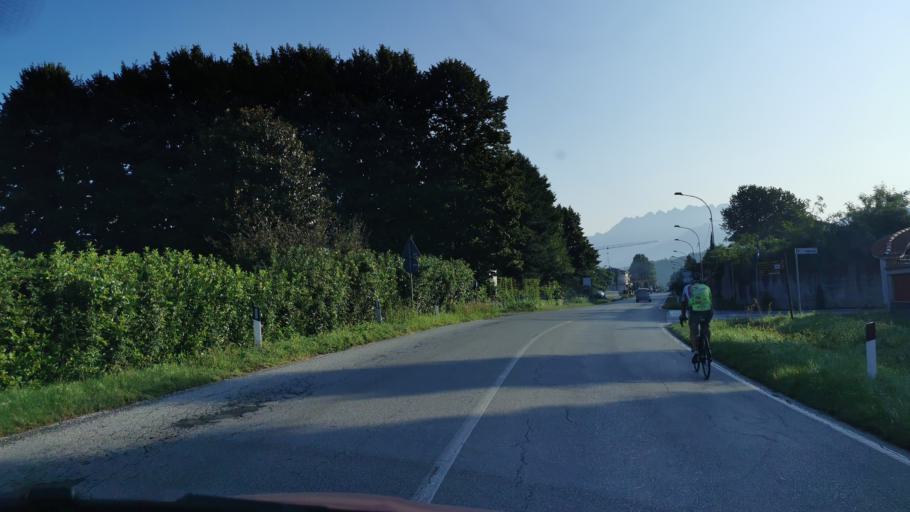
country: IT
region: Lombardy
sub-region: Provincia di Lecco
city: Oggiono
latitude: 45.7819
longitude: 9.3380
